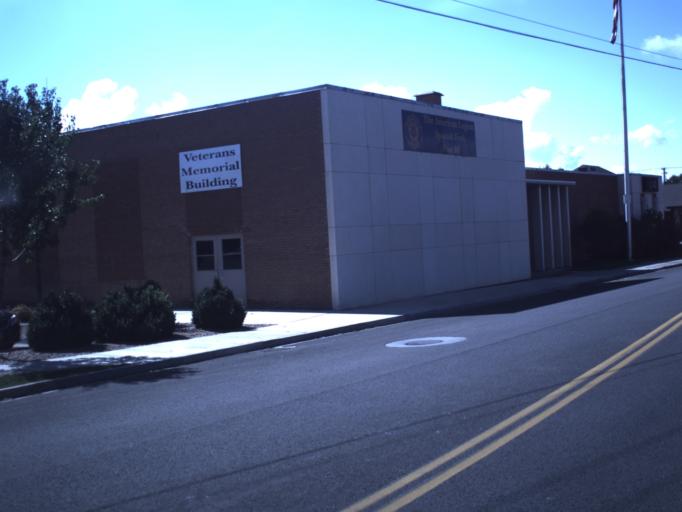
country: US
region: Utah
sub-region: Utah County
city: Spanish Fork
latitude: 40.1151
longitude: -111.6538
